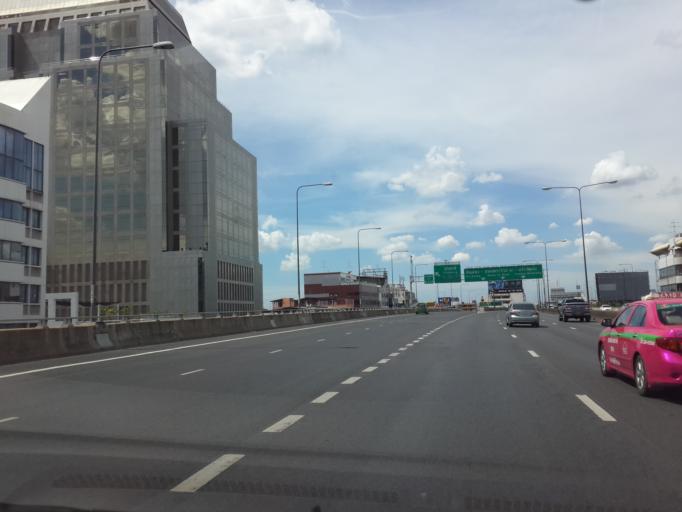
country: TH
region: Bangkok
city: Pathum Wan
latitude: 13.7467
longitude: 100.5207
